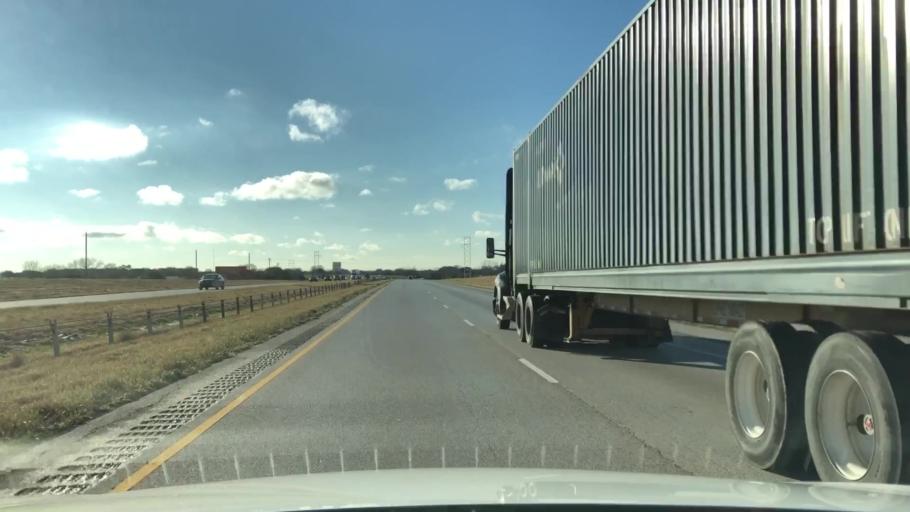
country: US
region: Texas
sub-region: Colorado County
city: Weimar
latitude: 29.6893
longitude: -96.6913
